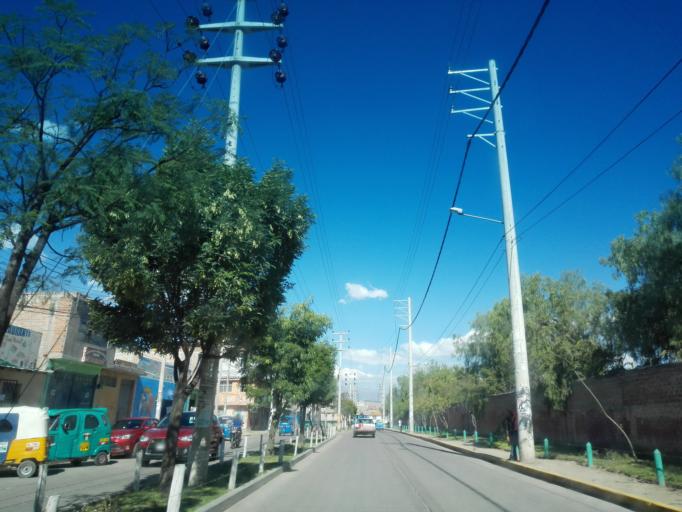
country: PE
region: Ayacucho
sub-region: Provincia de Huamanga
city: Ayacucho
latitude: -13.1546
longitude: -74.2203
